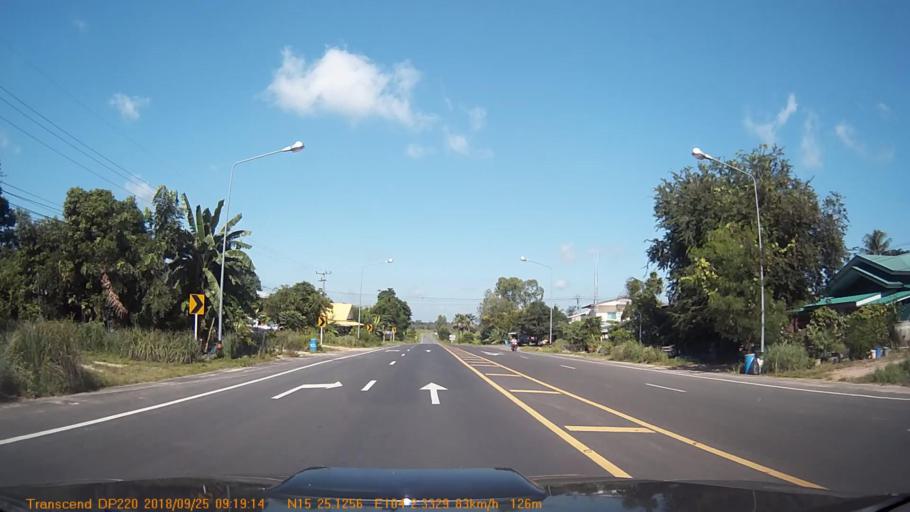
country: TH
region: Sisaket
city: Sila Lat
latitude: 15.4188
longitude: 104.0389
